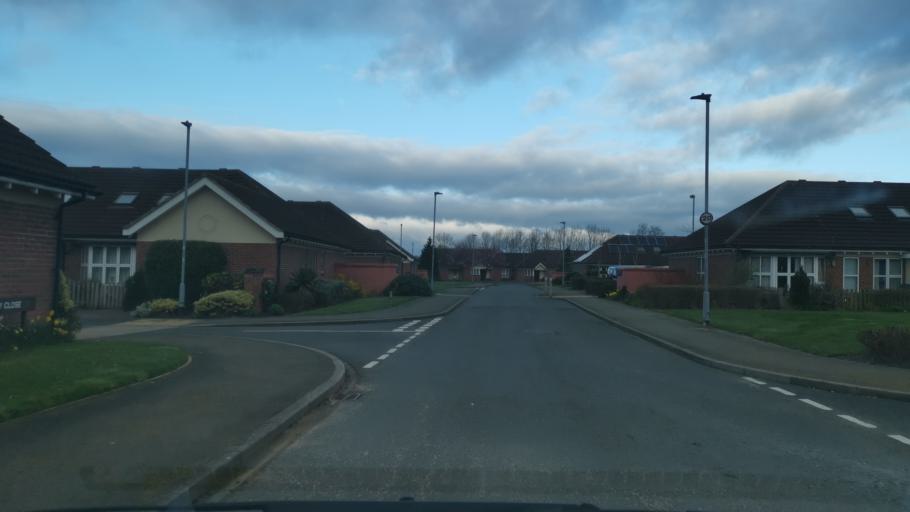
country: GB
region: England
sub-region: City of York
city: Haxby
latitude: 53.9953
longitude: -1.0743
